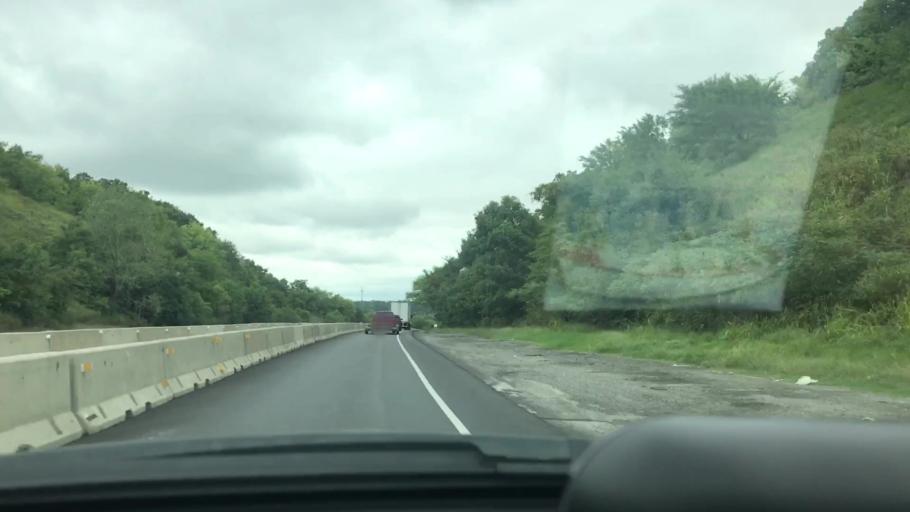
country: US
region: Oklahoma
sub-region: McIntosh County
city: Eufaula
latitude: 35.2719
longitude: -95.5925
